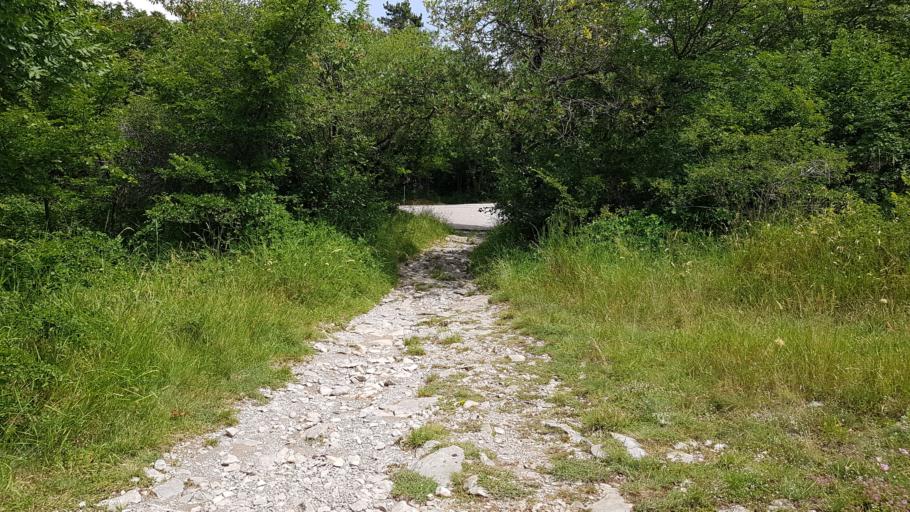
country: IT
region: Friuli Venezia Giulia
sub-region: Provincia di Trieste
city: Dolina
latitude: 45.6260
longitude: 13.8694
